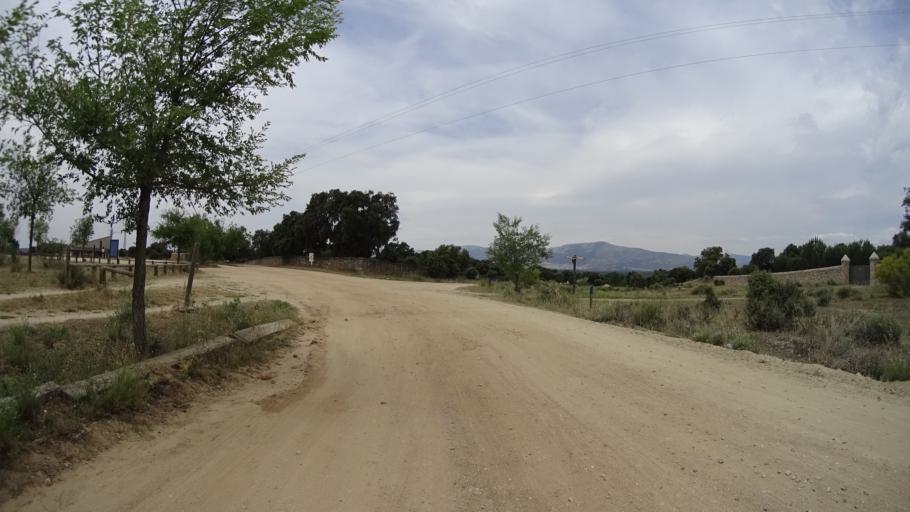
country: ES
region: Madrid
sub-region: Provincia de Madrid
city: Colmenarejo
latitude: 40.5699
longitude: -4.0313
